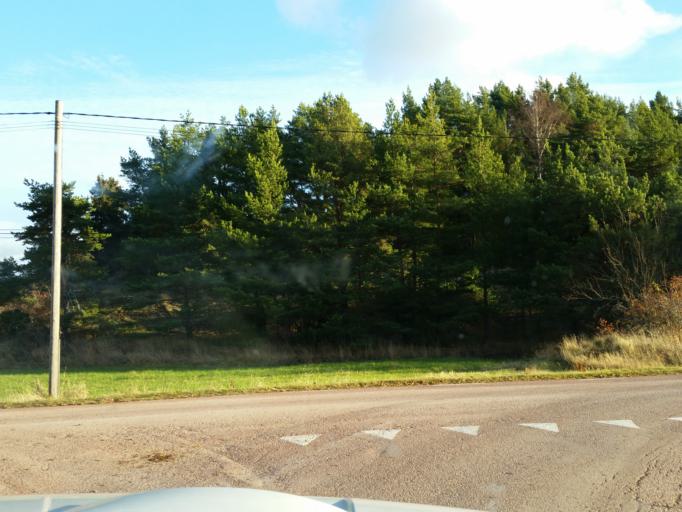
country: AX
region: Alands skaergard
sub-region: Foegloe
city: Foegloe
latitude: 60.0019
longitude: 20.3576
